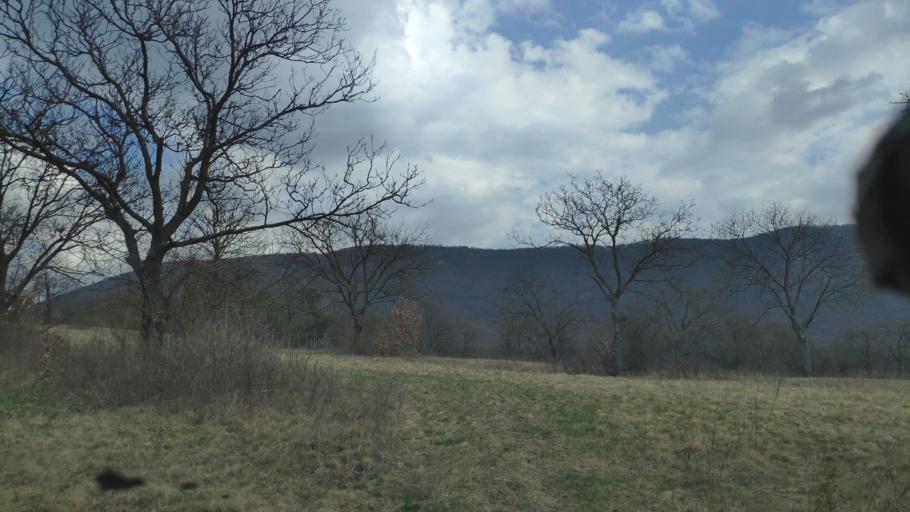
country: SK
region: Kosicky
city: Roznava
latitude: 48.6545
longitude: 20.3814
